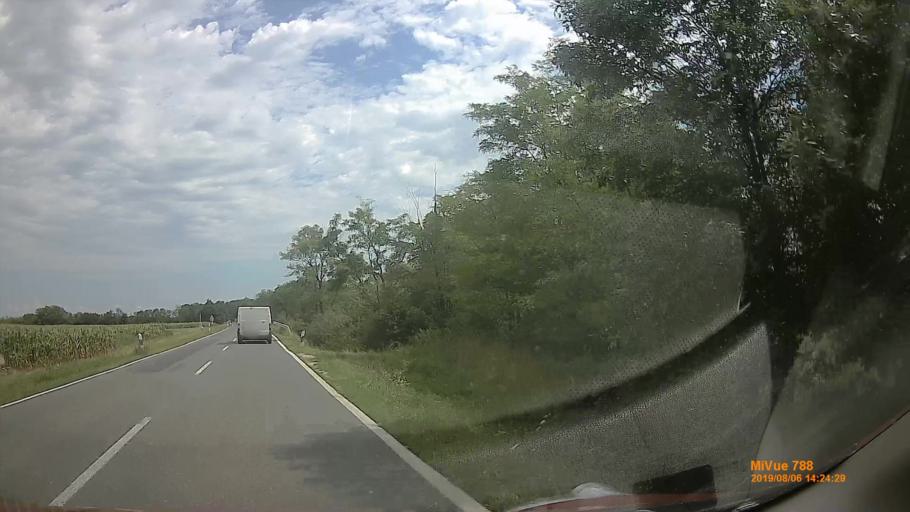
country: HU
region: Vas
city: Vasvar
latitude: 47.1476
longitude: 16.8199
